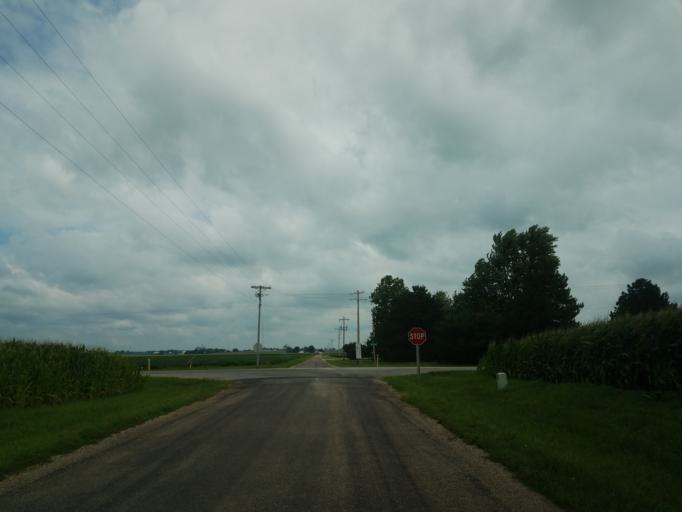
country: US
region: Illinois
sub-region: McLean County
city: Twin Grove
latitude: 40.4291
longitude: -89.0622
